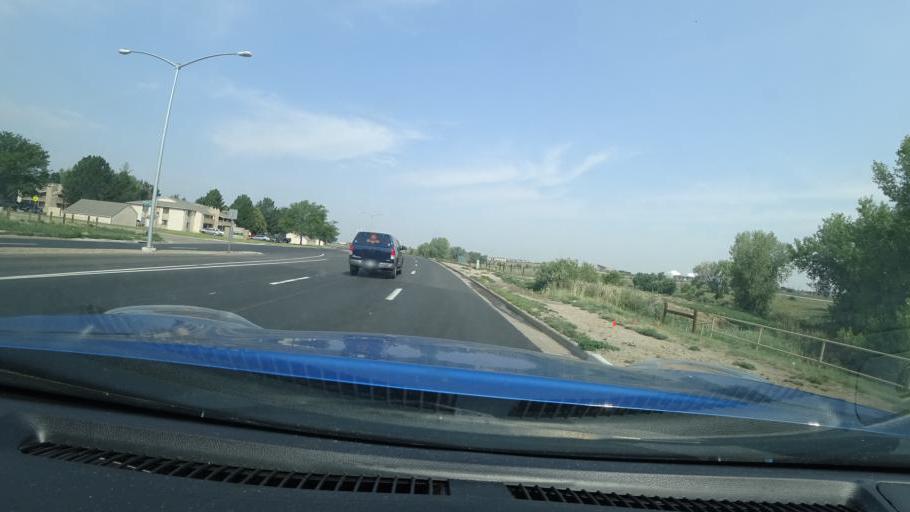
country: US
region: Colorado
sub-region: Adams County
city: Aurora
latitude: 39.7033
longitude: -104.7758
